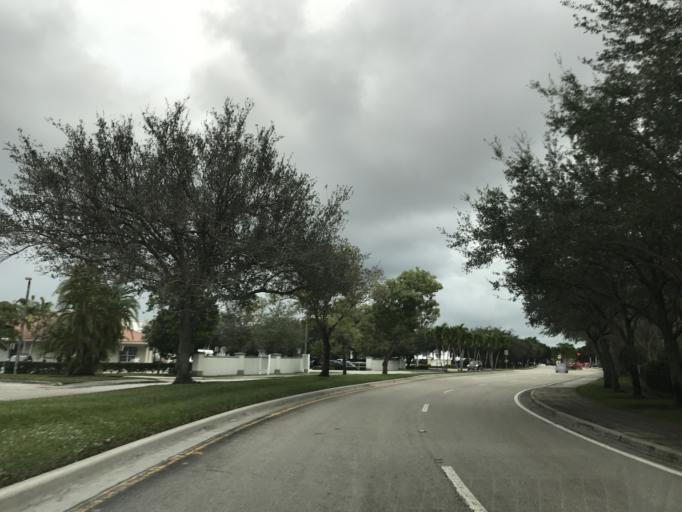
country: US
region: Florida
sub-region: Broward County
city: Coral Springs
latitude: 26.2993
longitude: -80.2818
